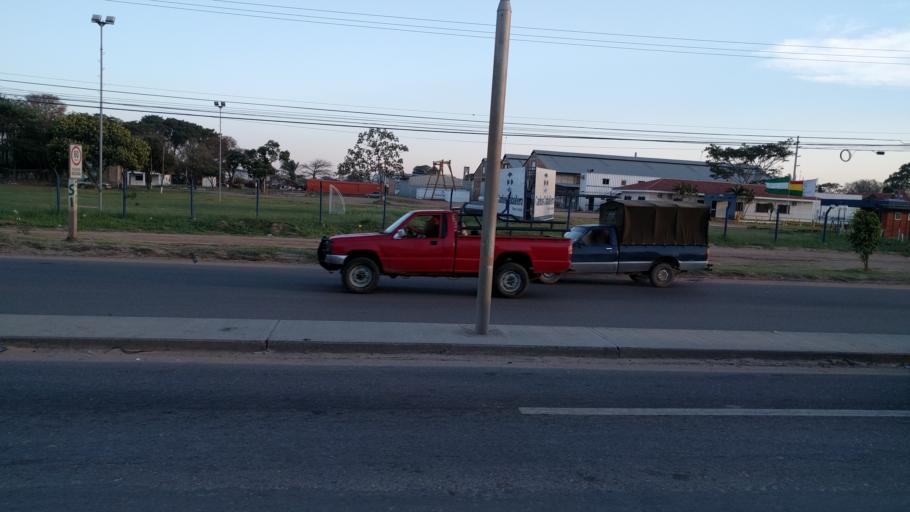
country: BO
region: Santa Cruz
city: Cotoca
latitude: -17.7643
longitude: -63.0990
